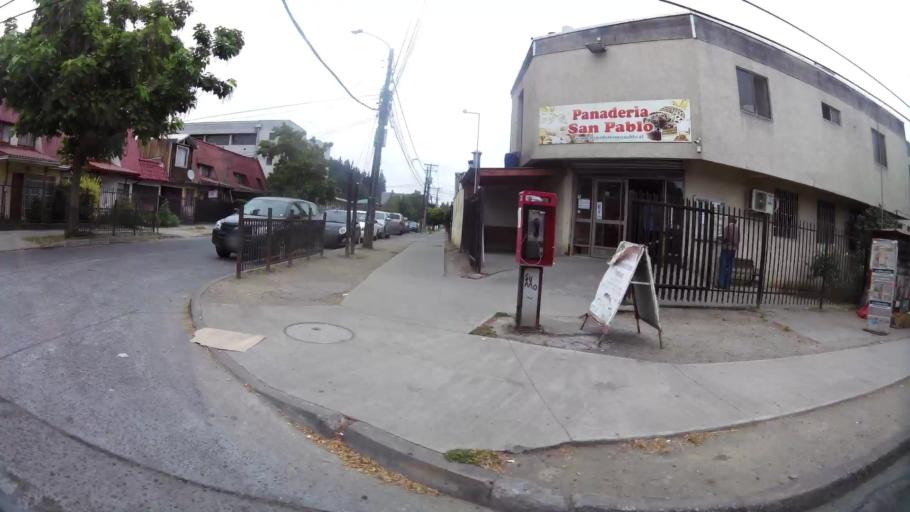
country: CL
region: Biobio
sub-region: Provincia de Concepcion
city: Concepcion
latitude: -36.8215
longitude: -73.0185
